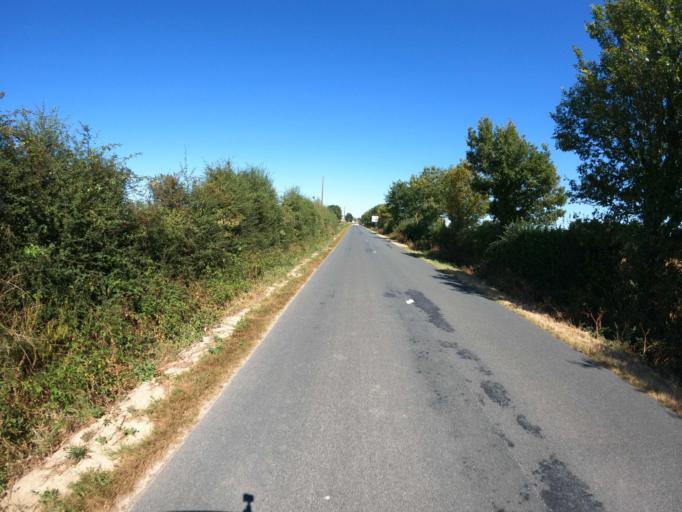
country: FR
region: Pays de la Loire
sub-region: Departement de la Vendee
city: Les Landes-Genusson
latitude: 46.9611
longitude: -1.1304
